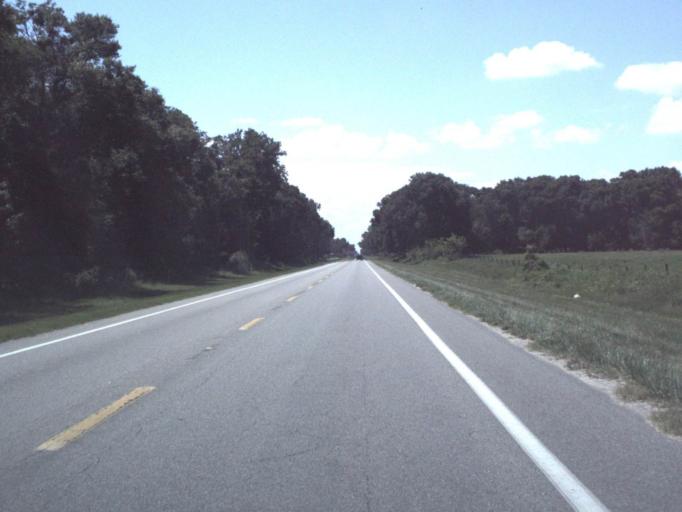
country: US
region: Florida
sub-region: Lafayette County
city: Mayo
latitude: 29.9709
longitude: -82.9818
